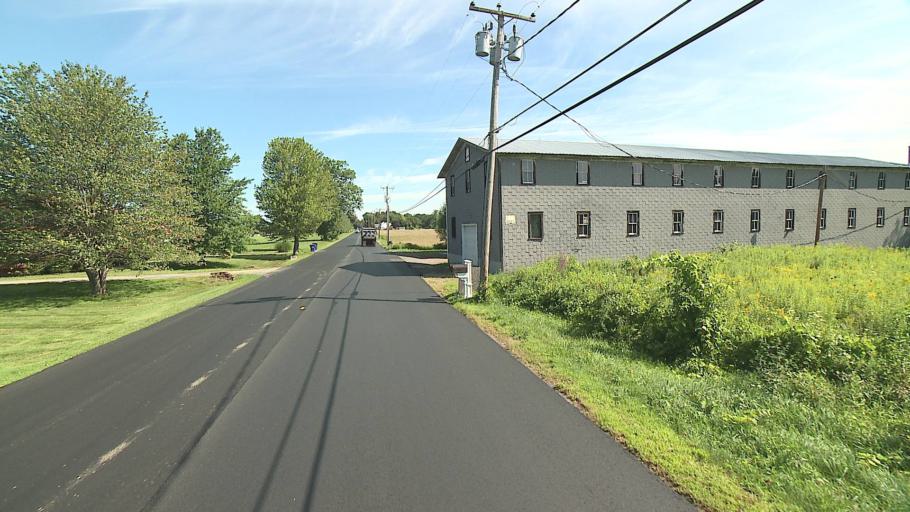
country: US
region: Connecticut
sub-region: Hartford County
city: Suffield Depot
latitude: 41.9801
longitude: -72.7066
